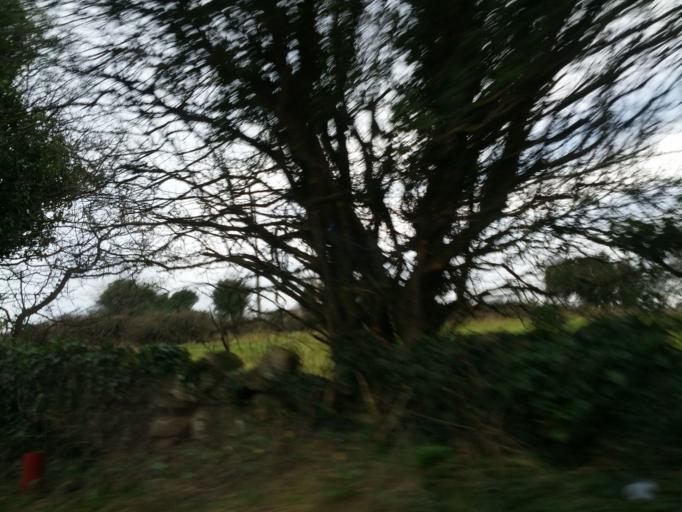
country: IE
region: Connaught
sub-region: County Galway
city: Gort
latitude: 53.1523
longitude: -8.8567
